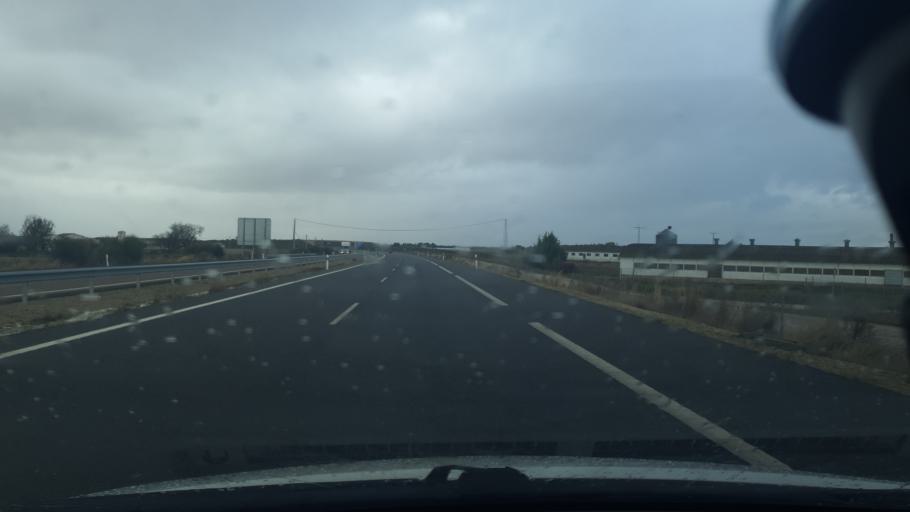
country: ES
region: Castille and Leon
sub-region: Provincia de Segovia
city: Cuellar
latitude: 41.4124
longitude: -4.3062
